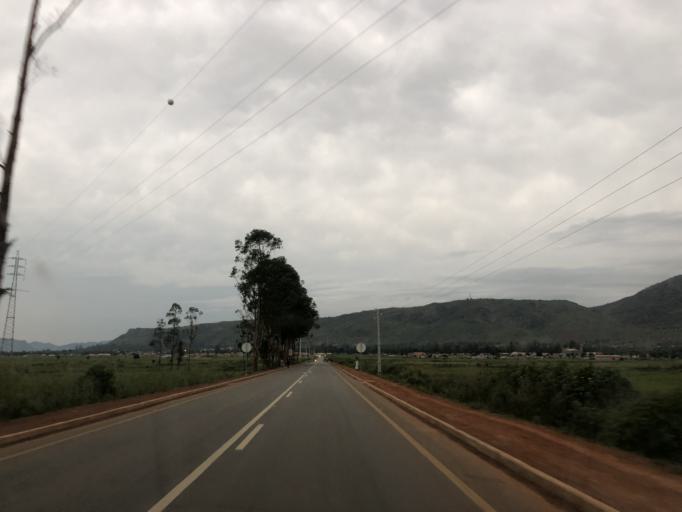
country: AO
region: Cuanza Sul
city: Uacu Cungo
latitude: -11.3367
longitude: 15.1029
